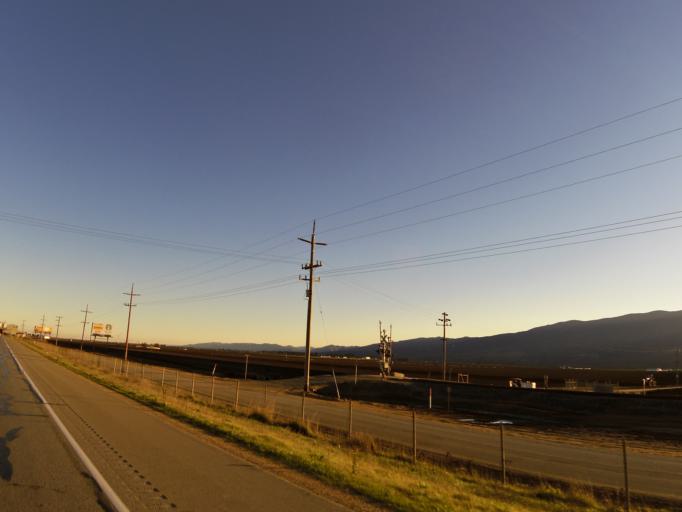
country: US
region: California
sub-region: Monterey County
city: Soledad
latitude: 36.4588
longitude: -121.3790
